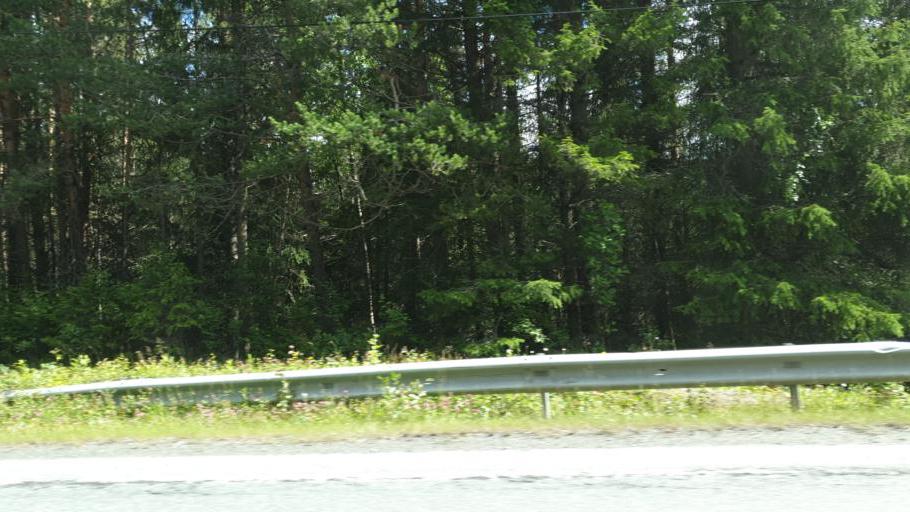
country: NO
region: Sor-Trondelag
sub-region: Rennebu
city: Berkak
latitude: 62.7073
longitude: 9.9539
